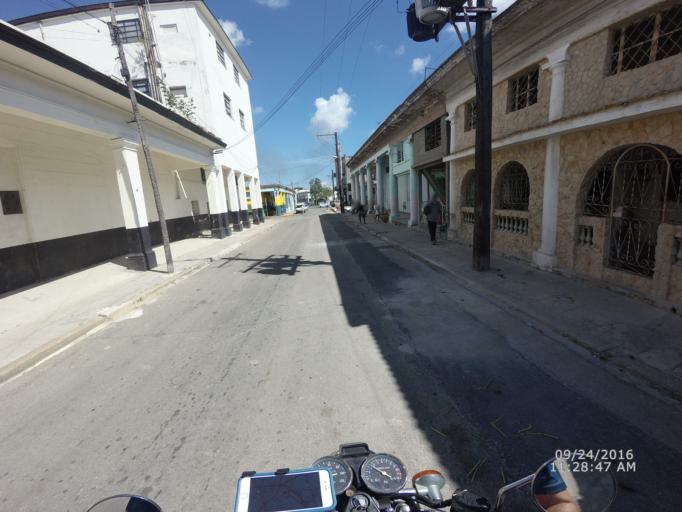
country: CU
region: La Habana
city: Cerro
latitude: 23.1132
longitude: -82.3646
